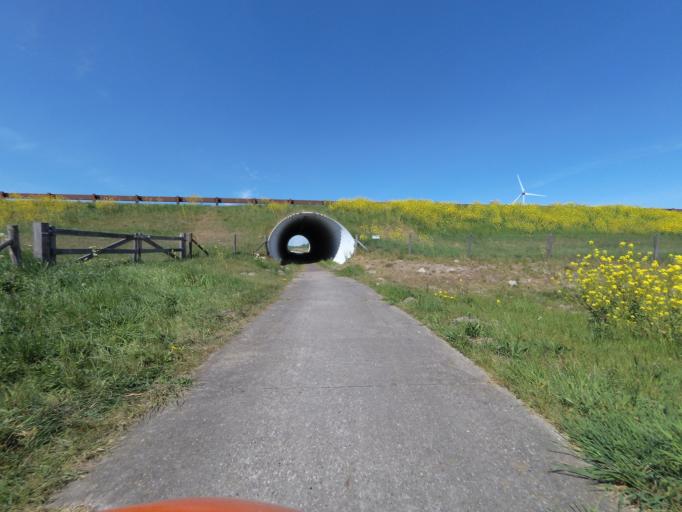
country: NL
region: Flevoland
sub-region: Gemeente Zeewolde
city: Zeewolde
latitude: 52.3773
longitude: 5.5477
